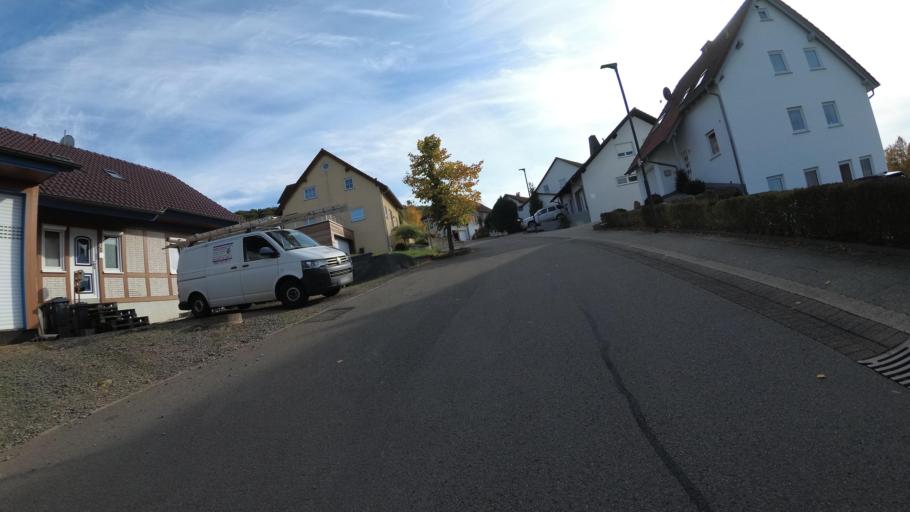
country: DE
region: Rheinland-Pfalz
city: Borsborn
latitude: 49.4528
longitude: 7.3879
